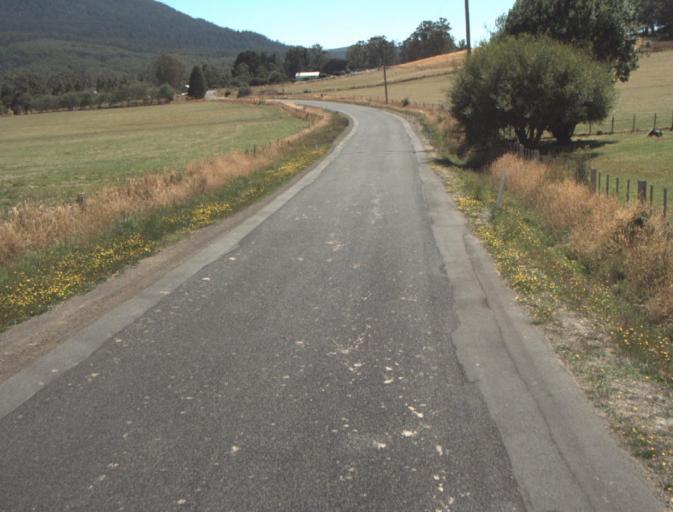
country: AU
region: Tasmania
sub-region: Launceston
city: Newstead
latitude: -41.3442
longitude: 147.3033
